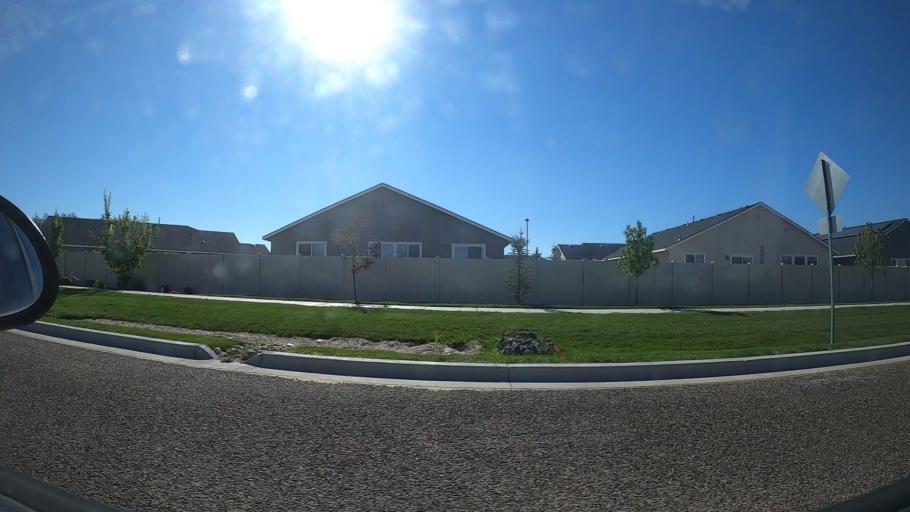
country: US
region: Idaho
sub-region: Canyon County
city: Nampa
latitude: 43.5655
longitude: -116.6130
